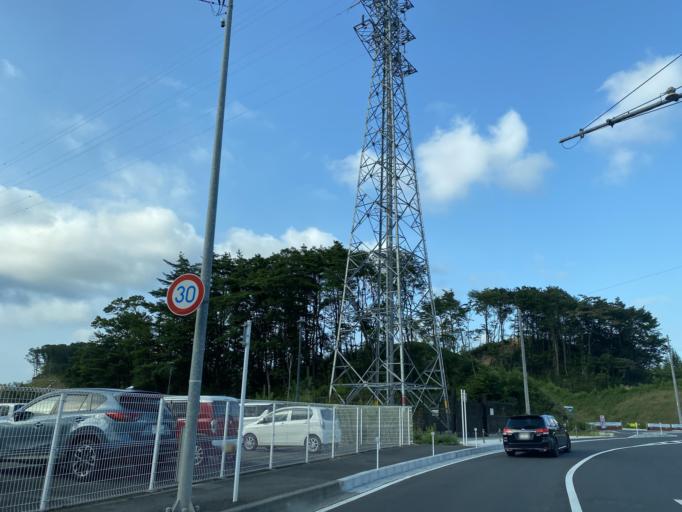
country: JP
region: Miyagi
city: Tomiya
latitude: 38.3667
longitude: 140.8587
